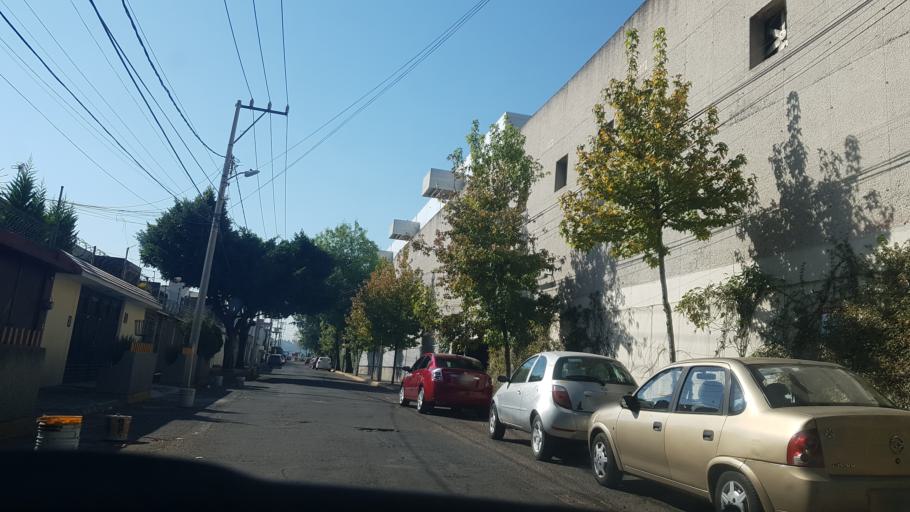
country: MX
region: Mexico
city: Naucalpan de Juarez
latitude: 19.4966
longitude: -99.2463
